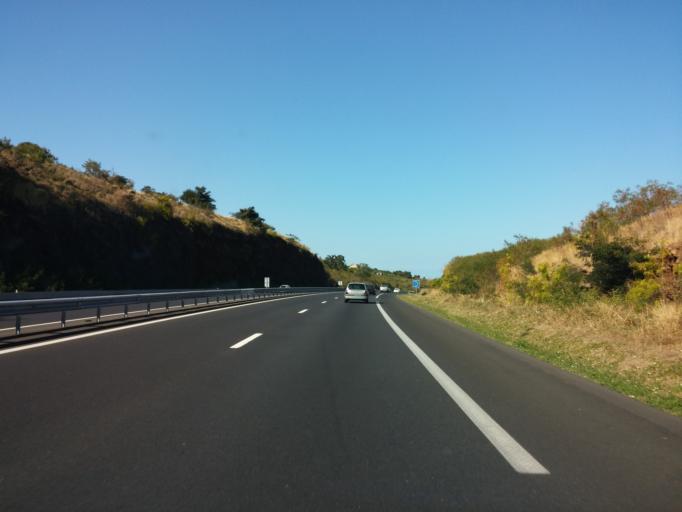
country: RE
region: Reunion
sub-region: Reunion
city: Saint-Leu
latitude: -21.1674
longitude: 55.2984
